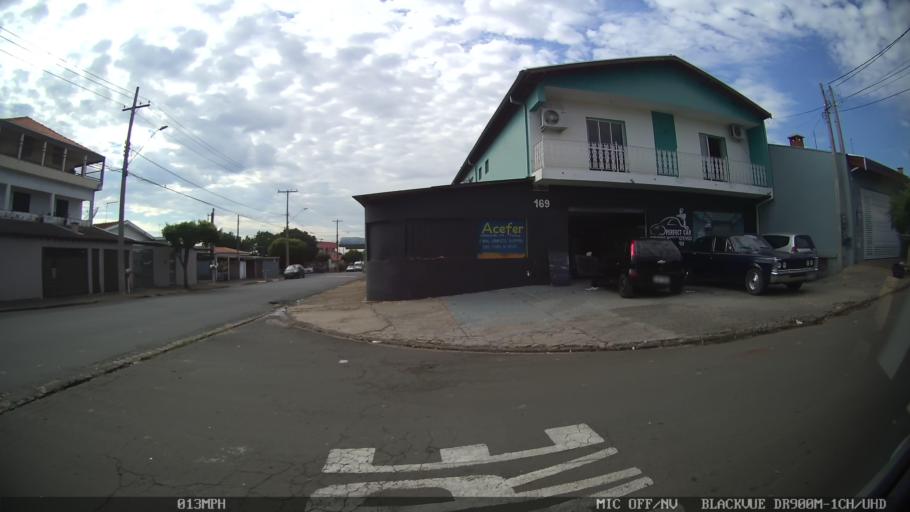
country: BR
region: Sao Paulo
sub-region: Americana
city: Americana
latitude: -22.7202
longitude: -47.3602
